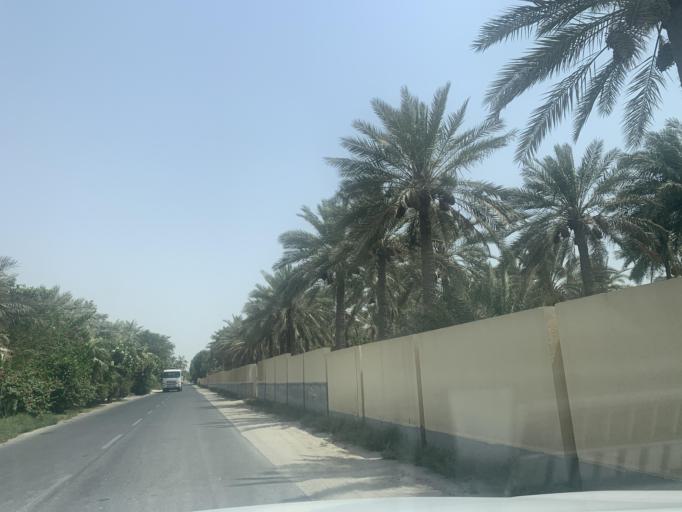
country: BH
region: Manama
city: Jidd Hafs
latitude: 26.2279
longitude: 50.4659
